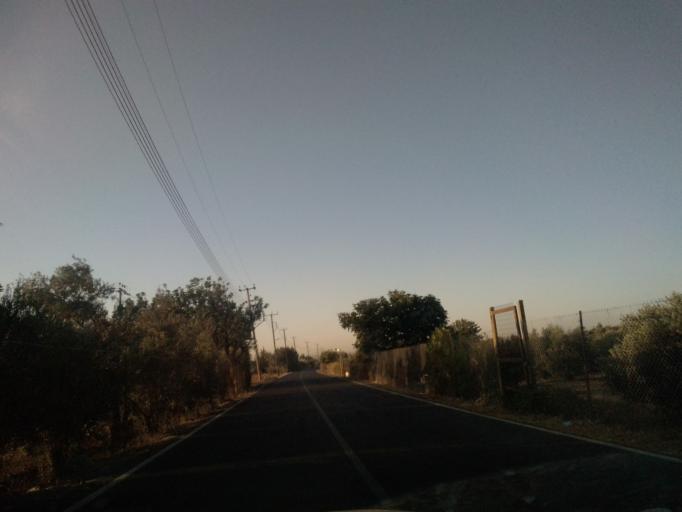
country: CY
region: Limassol
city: Ypsonas
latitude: 34.6775
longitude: 32.9569
